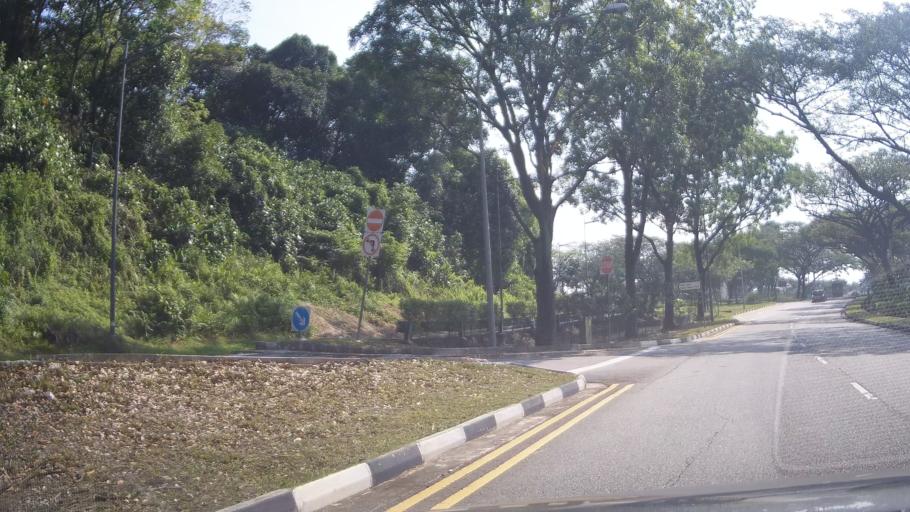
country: MY
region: Johor
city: Johor Bahru
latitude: 1.3302
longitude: 103.6716
